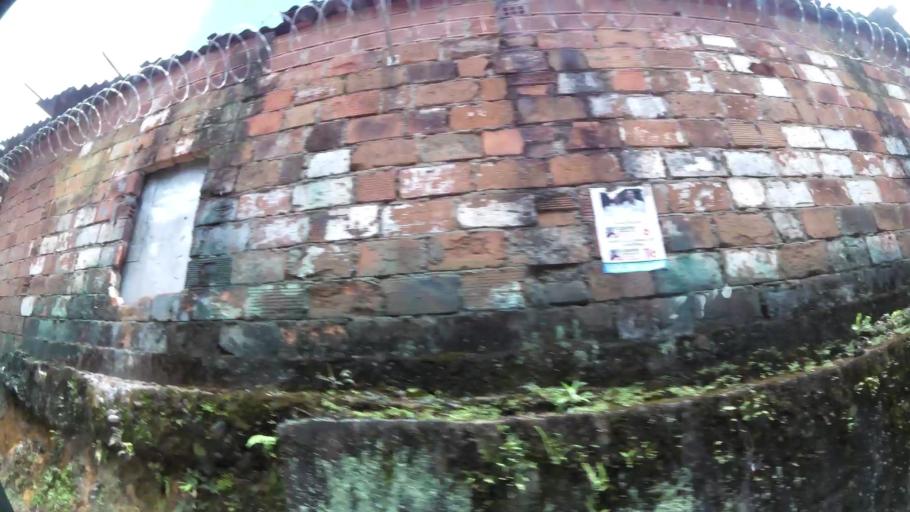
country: CO
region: Antioquia
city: La Estrella
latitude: 6.1563
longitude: -75.6304
